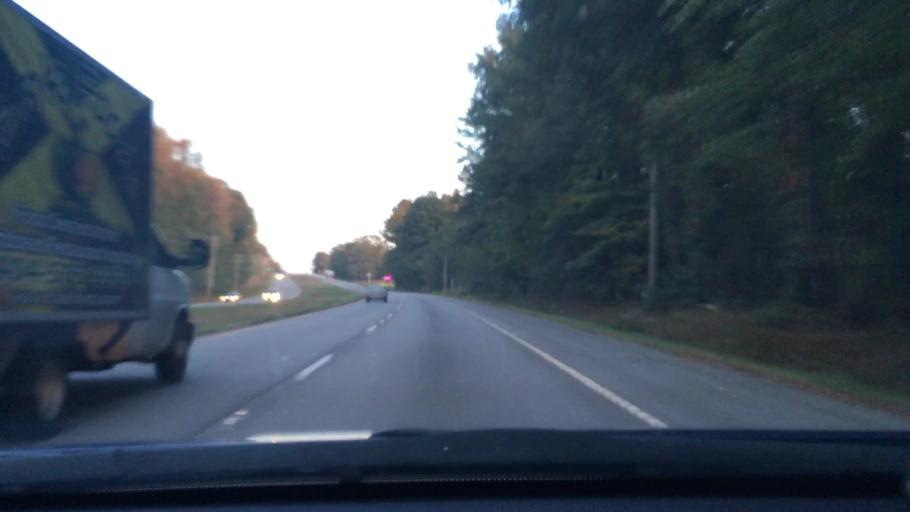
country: US
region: South Carolina
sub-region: Richland County
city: Gadsden
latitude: 33.9441
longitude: -80.7500
